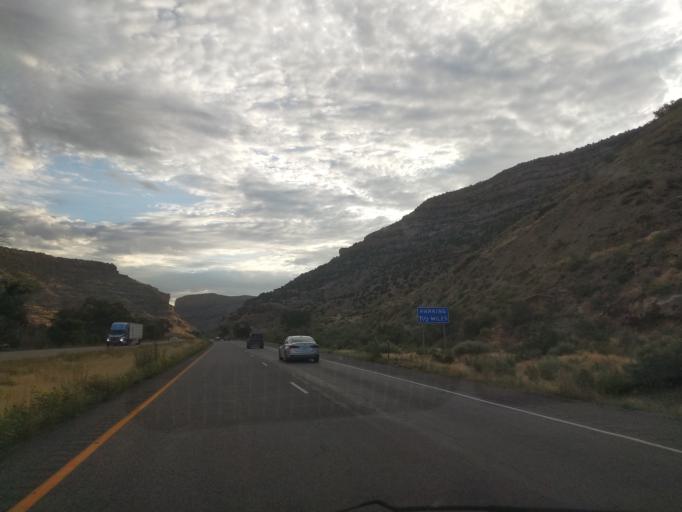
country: US
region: Colorado
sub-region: Mesa County
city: Palisade
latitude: 39.1679
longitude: -108.2981
